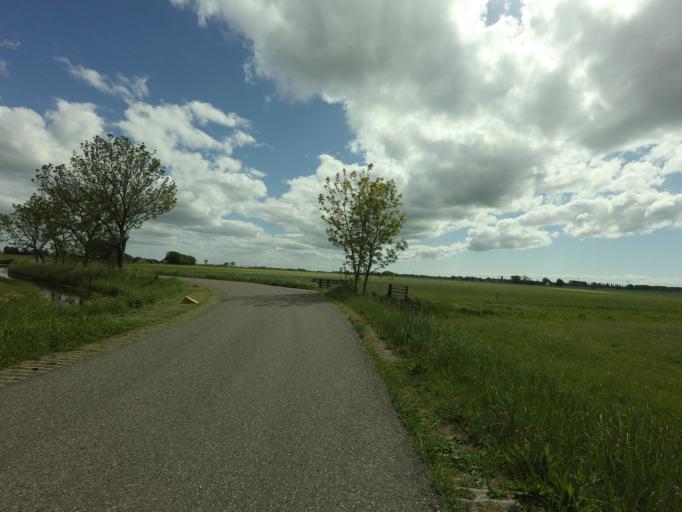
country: NL
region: Friesland
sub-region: Sudwest Fryslan
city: Bolsward
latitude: 53.0836
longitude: 5.5479
